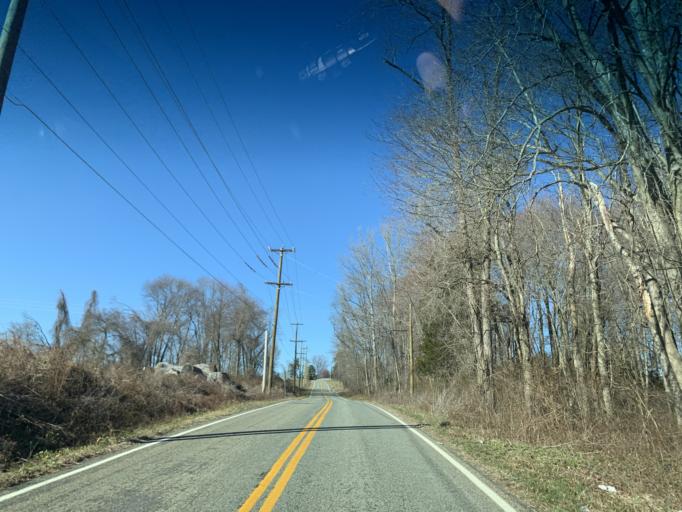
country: US
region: Maryland
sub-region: Cecil County
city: Rising Sun
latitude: 39.6778
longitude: -76.0990
